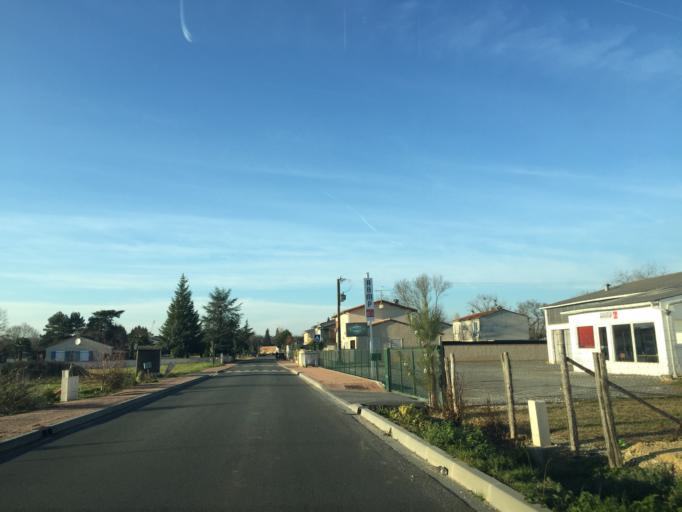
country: FR
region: Aquitaine
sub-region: Departement de la Dordogne
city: Saint-Aulaye
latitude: 45.2590
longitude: 0.1953
